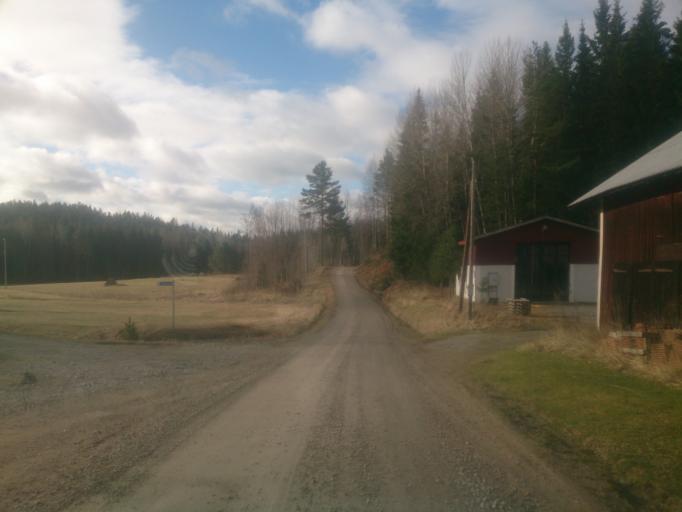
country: SE
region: OEstergoetland
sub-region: Atvidabergs Kommun
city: Atvidaberg
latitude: 58.2270
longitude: 16.1758
